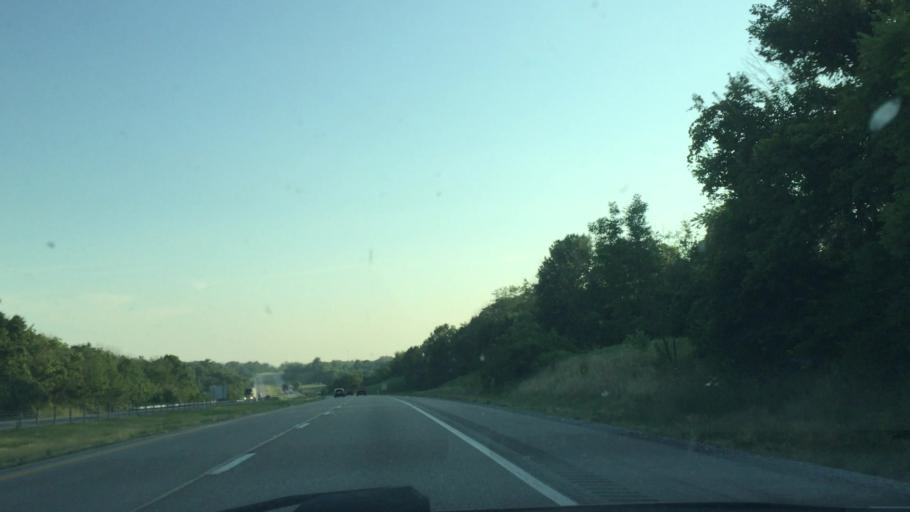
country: US
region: Kentucky
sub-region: Boone County
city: Verona
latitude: 38.8276
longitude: -84.6934
